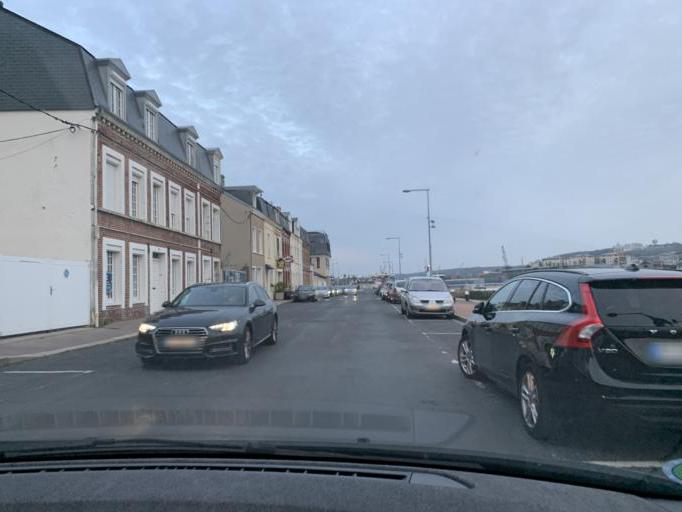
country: FR
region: Haute-Normandie
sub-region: Departement de la Seine-Maritime
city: Fecamp
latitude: 49.7628
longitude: 0.3721
